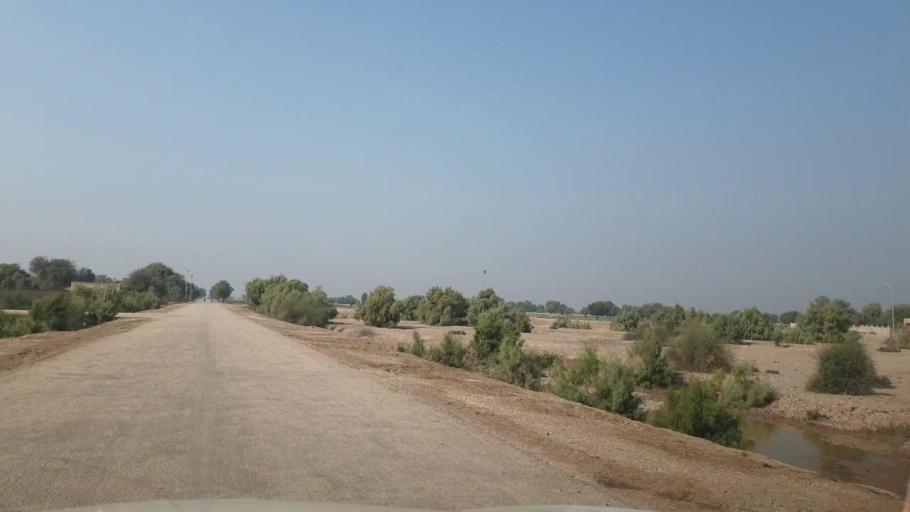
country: PK
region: Sindh
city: Bhan
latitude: 26.5076
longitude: 67.7902
